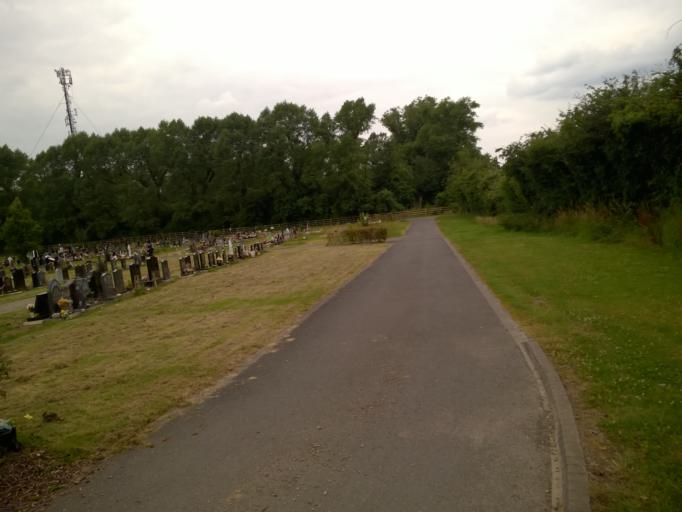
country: GB
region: England
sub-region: Leicestershire
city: Anstey
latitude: 52.6547
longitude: -1.1667
